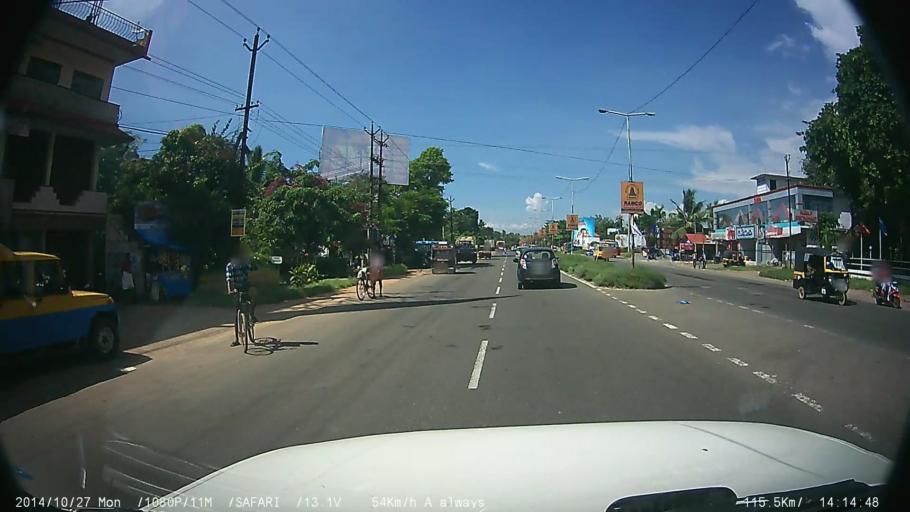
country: IN
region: Kerala
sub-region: Alappuzha
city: Kutiatodu
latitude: 9.8265
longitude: 76.3104
